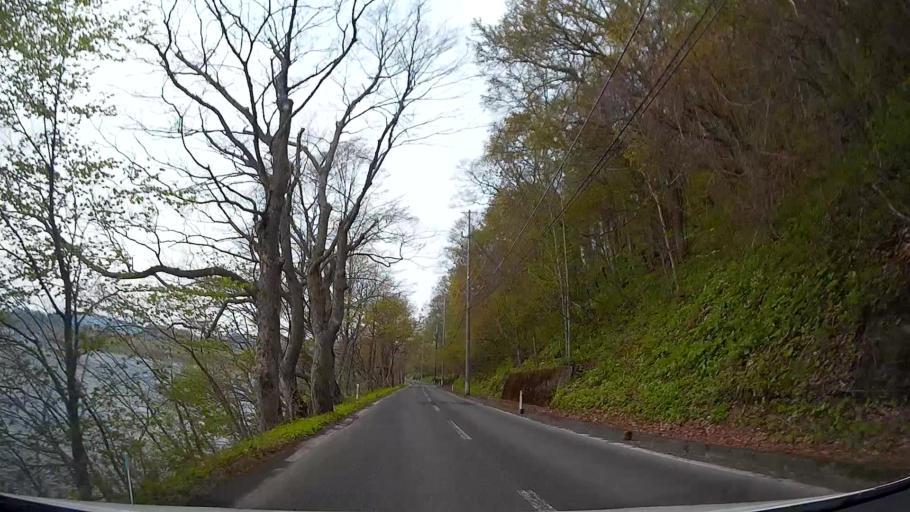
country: JP
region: Akita
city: Hanawa
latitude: 40.4187
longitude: 140.8896
